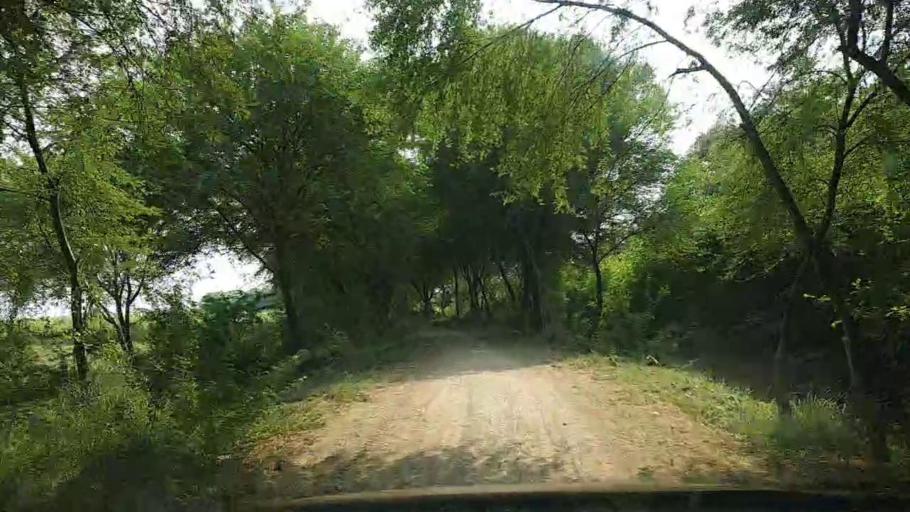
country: PK
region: Sindh
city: Mirpur Batoro
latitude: 24.6905
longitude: 68.2211
